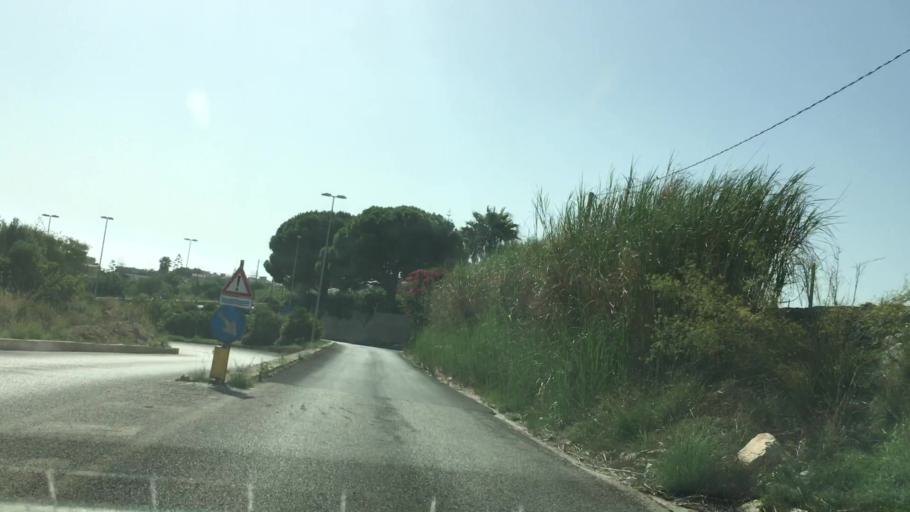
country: IT
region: Sicily
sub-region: Ragusa
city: Pozzallo
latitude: 36.7165
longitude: 14.7860
